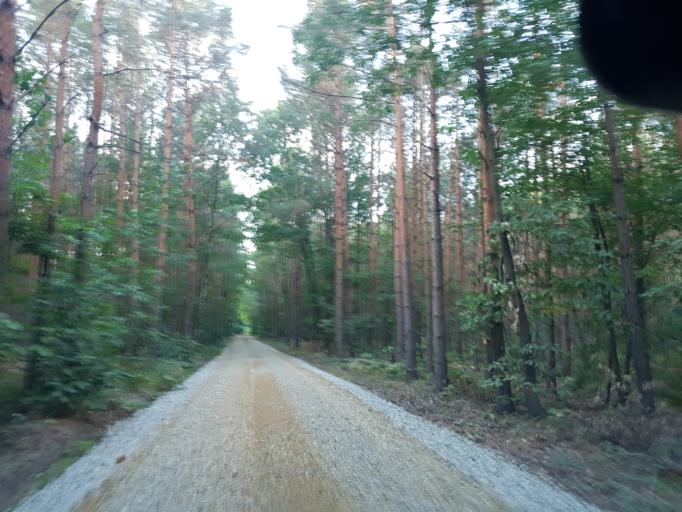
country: DE
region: Brandenburg
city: Hohenleipisch
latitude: 51.5298
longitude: 13.5834
